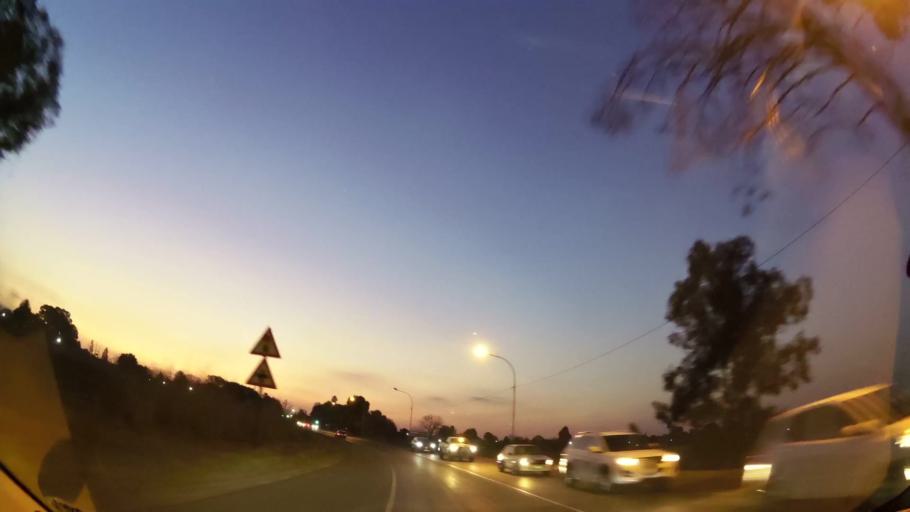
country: ZA
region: Gauteng
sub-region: Ekurhuleni Metropolitan Municipality
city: Benoni
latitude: -26.0985
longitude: 28.3131
